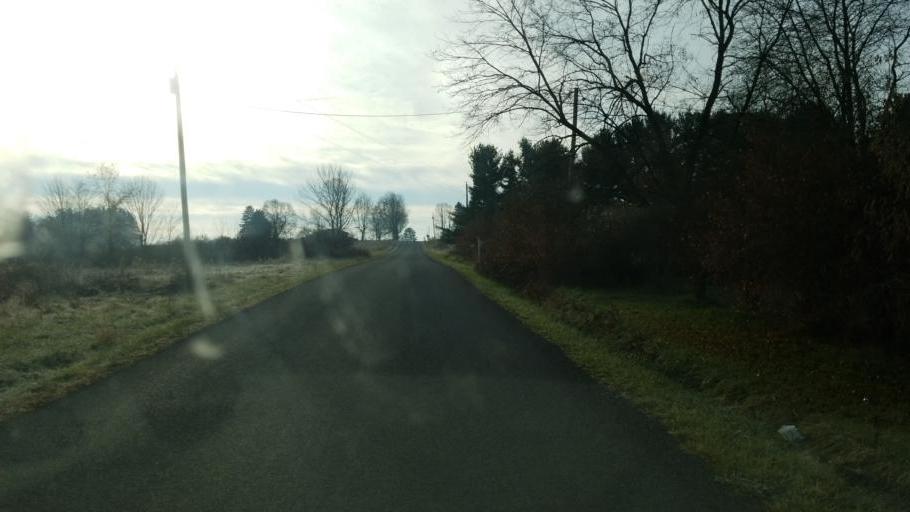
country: US
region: Pennsylvania
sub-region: Crawford County
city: Cochranton
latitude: 41.5019
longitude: -80.1148
